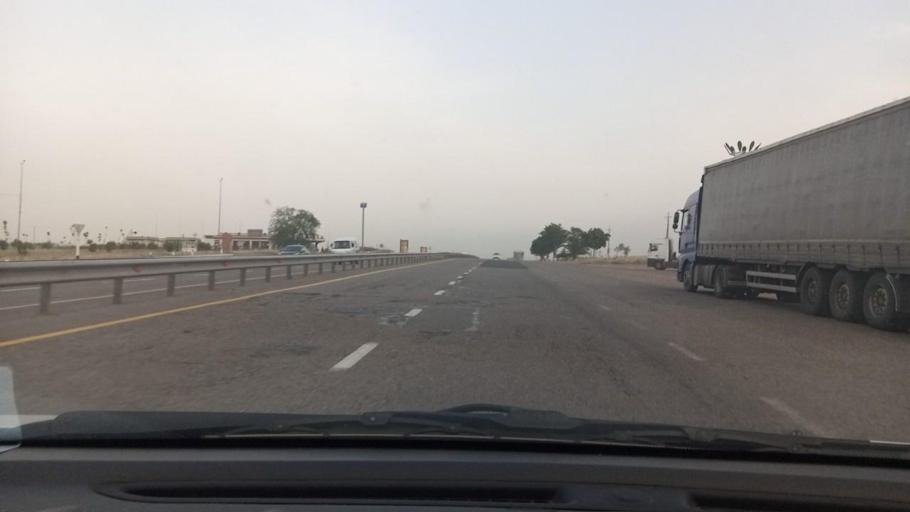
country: UZ
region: Toshkent
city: Ohangaron
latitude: 40.9430
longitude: 69.5795
